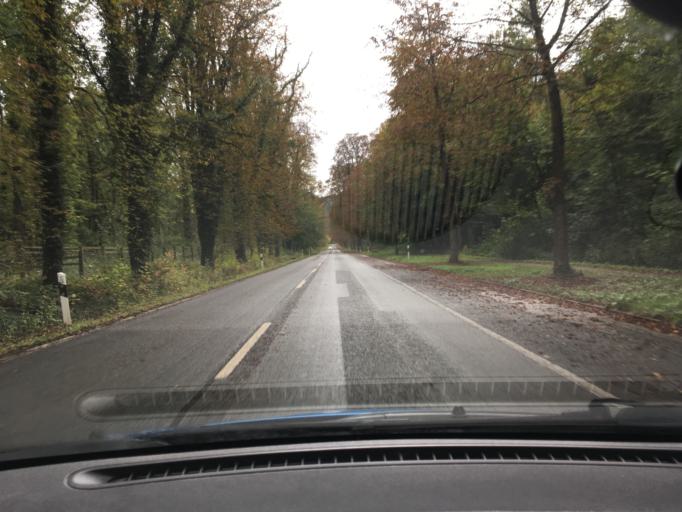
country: DE
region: Lower Saxony
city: Springe
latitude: 52.1853
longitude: 9.6027
